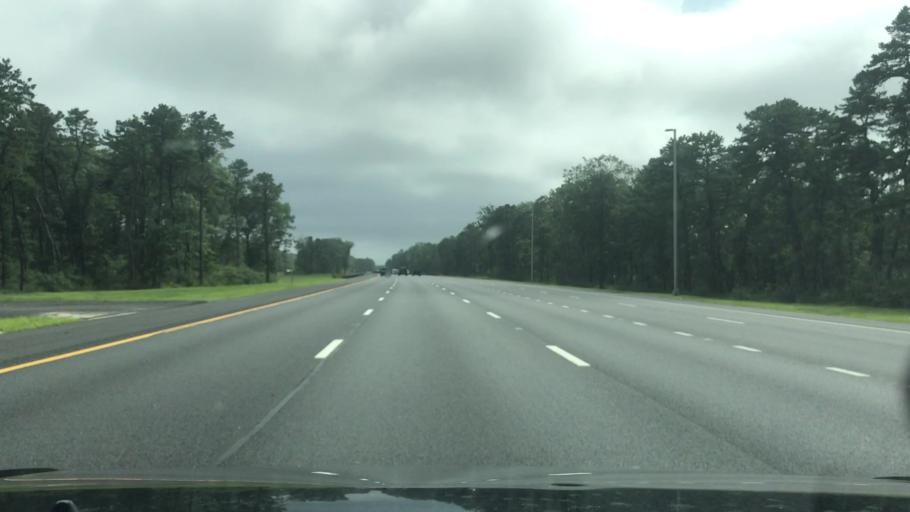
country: US
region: New Jersey
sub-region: Ocean County
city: Leisure Village
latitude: 40.0475
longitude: -74.1741
